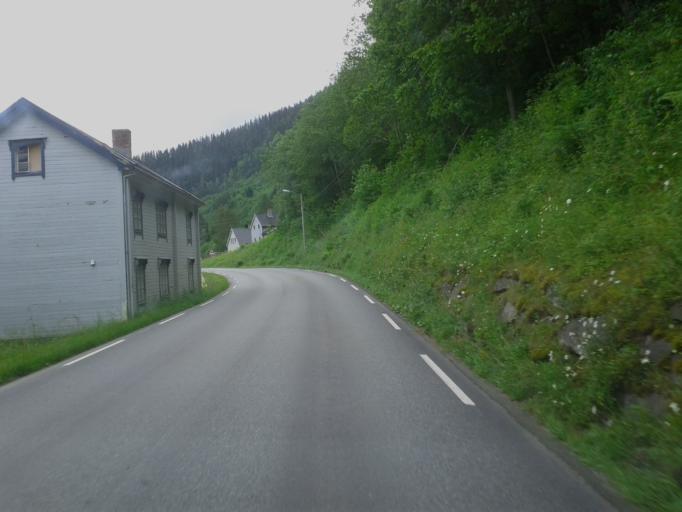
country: NO
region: Sor-Trondelag
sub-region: Midtre Gauldal
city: Storen
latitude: 62.9750
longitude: 10.5575
